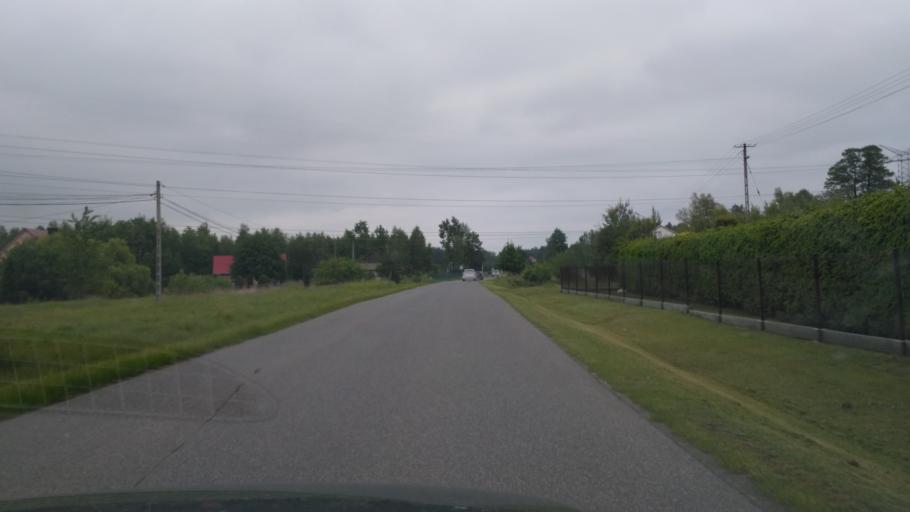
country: PL
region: Subcarpathian Voivodeship
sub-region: Powiat ropczycko-sedziszowski
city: Sedziszow Malopolski
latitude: 50.1358
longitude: 21.6690
